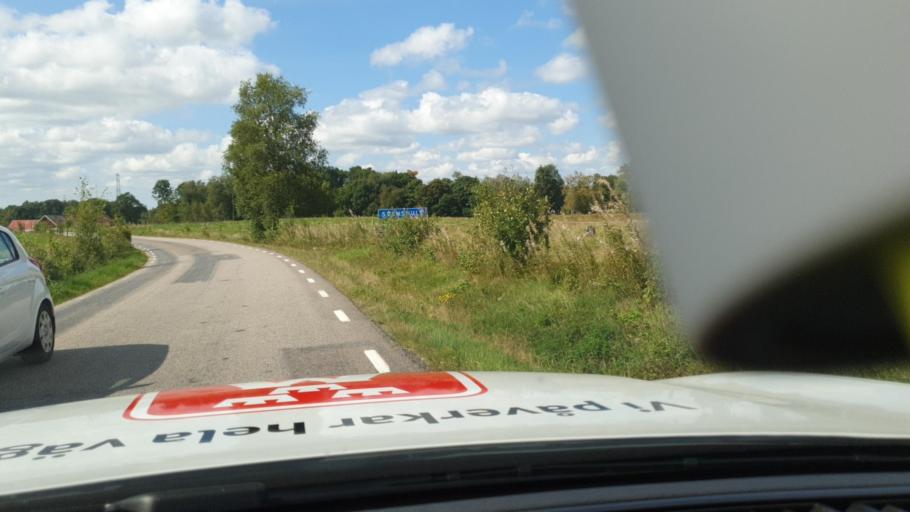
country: SE
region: Halland
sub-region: Laholms Kommun
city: Knared
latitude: 56.4801
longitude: 13.2624
